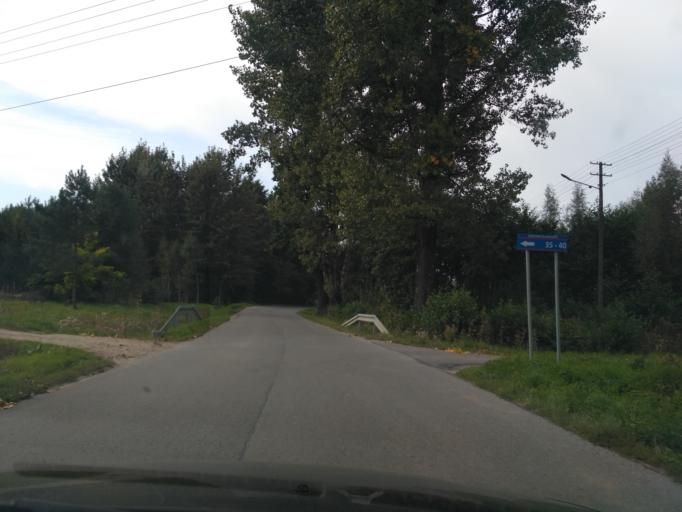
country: PL
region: Subcarpathian Voivodeship
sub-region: Powiat rzeszowski
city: Zglobien
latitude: 50.0354
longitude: 21.8416
